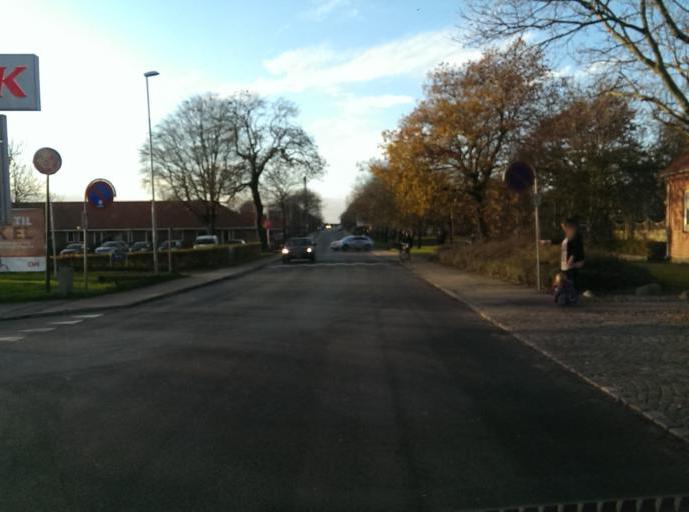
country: DK
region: South Denmark
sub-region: Esbjerg Kommune
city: Tjaereborg
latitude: 55.4633
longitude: 8.5846
